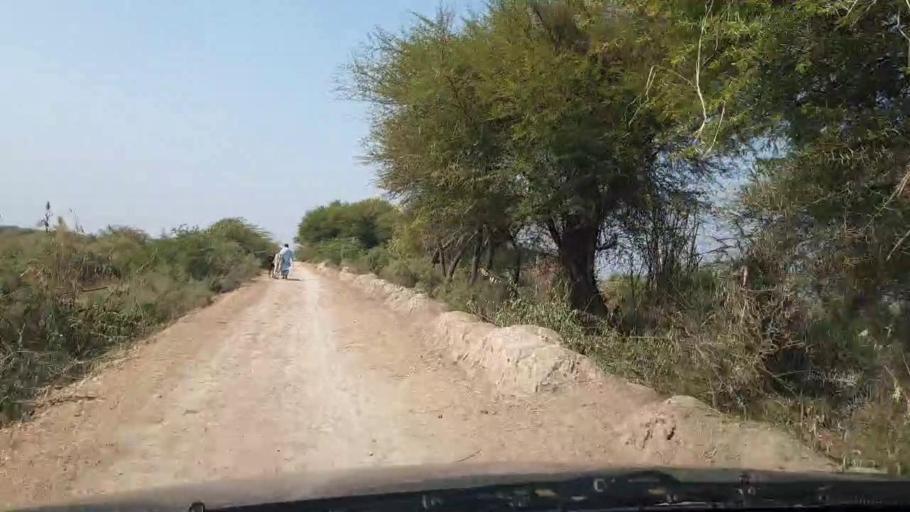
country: PK
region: Sindh
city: Jhol
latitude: 25.8858
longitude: 68.9881
